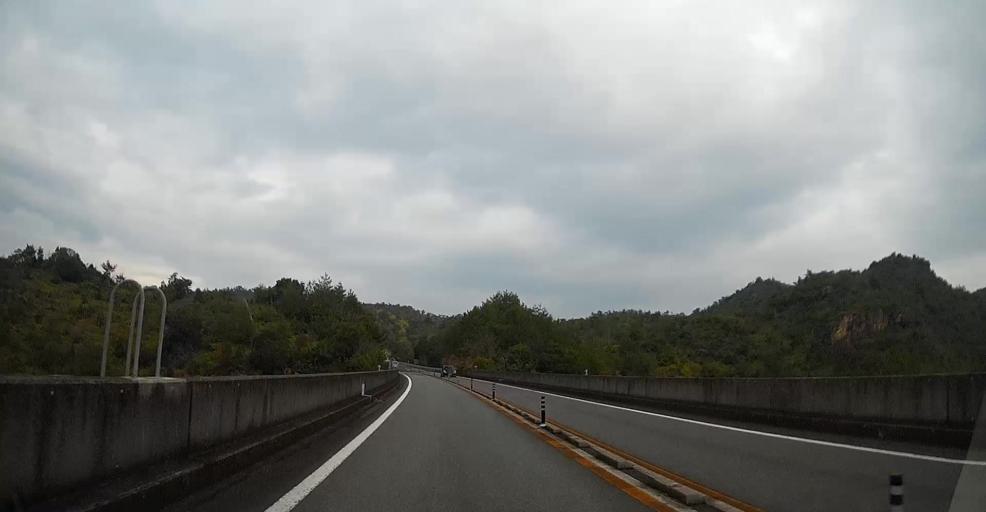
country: JP
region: Kumamoto
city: Yatsushiro
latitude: 32.5133
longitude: 130.4124
